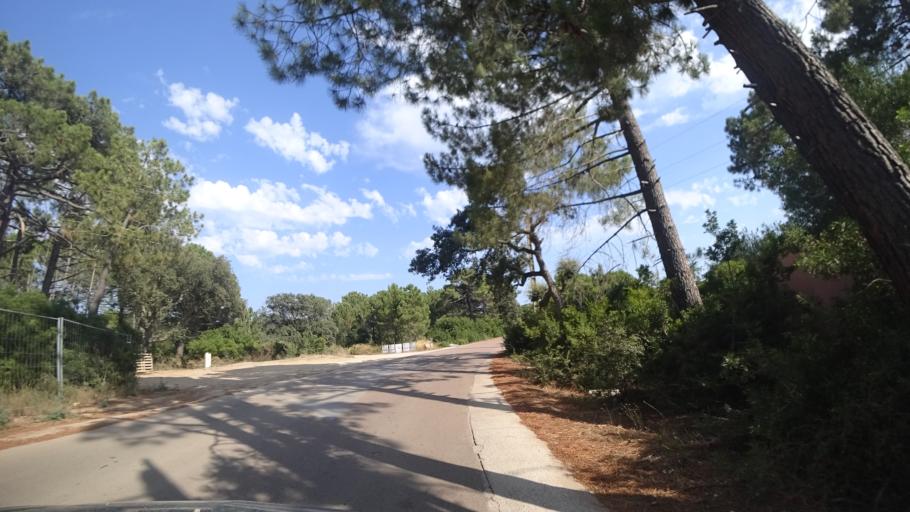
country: FR
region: Corsica
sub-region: Departement de la Corse-du-Sud
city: Porto-Vecchio
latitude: 41.6273
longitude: 9.3355
